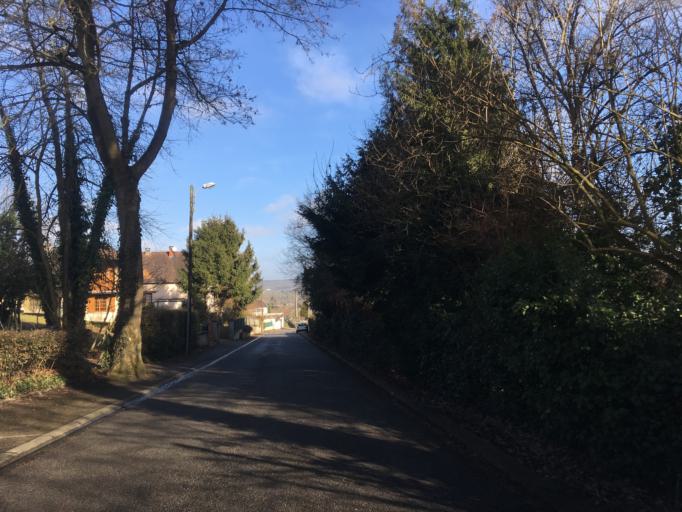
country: FR
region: Haute-Normandie
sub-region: Departement de l'Eure
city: Saint-Just
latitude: 49.1080
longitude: 1.4353
